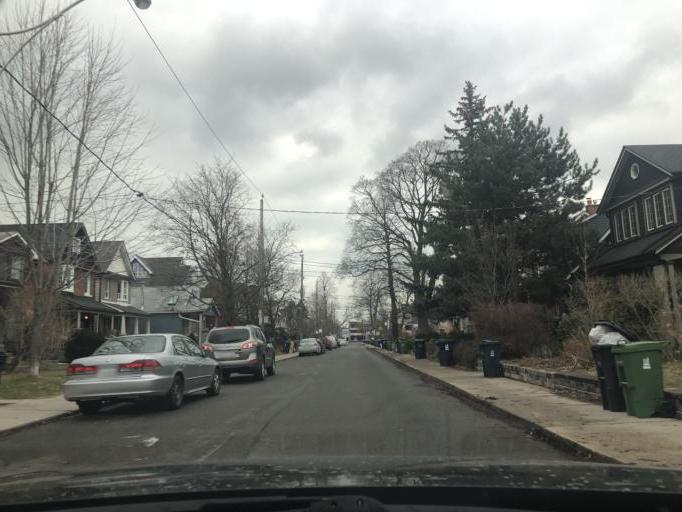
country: CA
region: Ontario
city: Toronto
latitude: 43.6805
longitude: -79.3517
